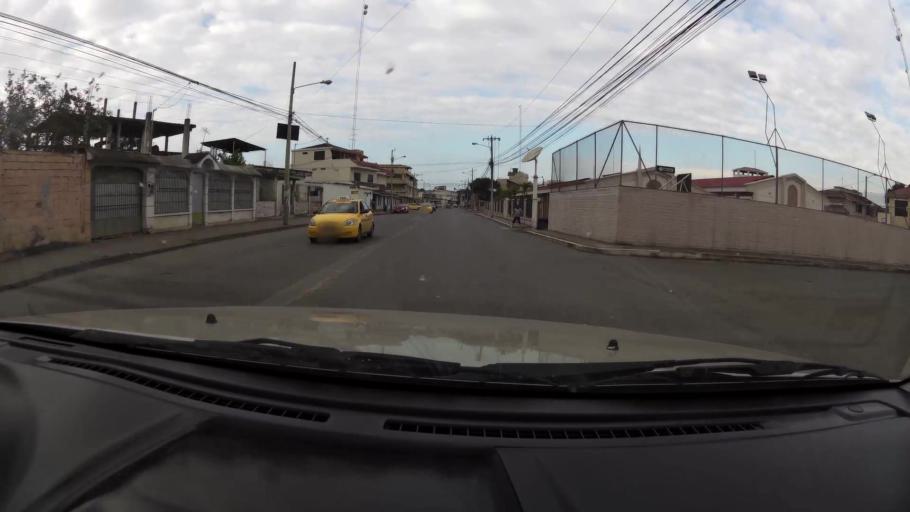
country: EC
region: El Oro
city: Machala
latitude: -3.2646
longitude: -79.9482
